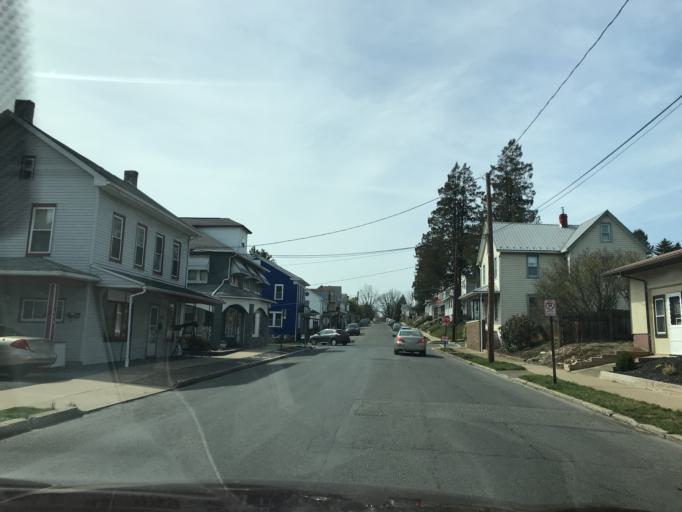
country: US
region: Pennsylvania
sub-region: Northumberland County
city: Northumberland
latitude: 40.8926
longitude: -76.8029
